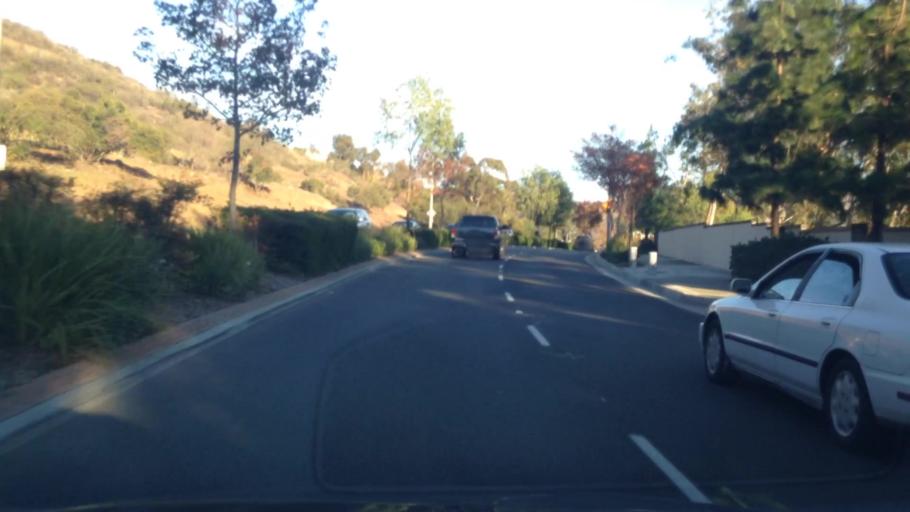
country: US
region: California
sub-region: Orange County
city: Villa Park
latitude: 33.8220
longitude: -117.7903
